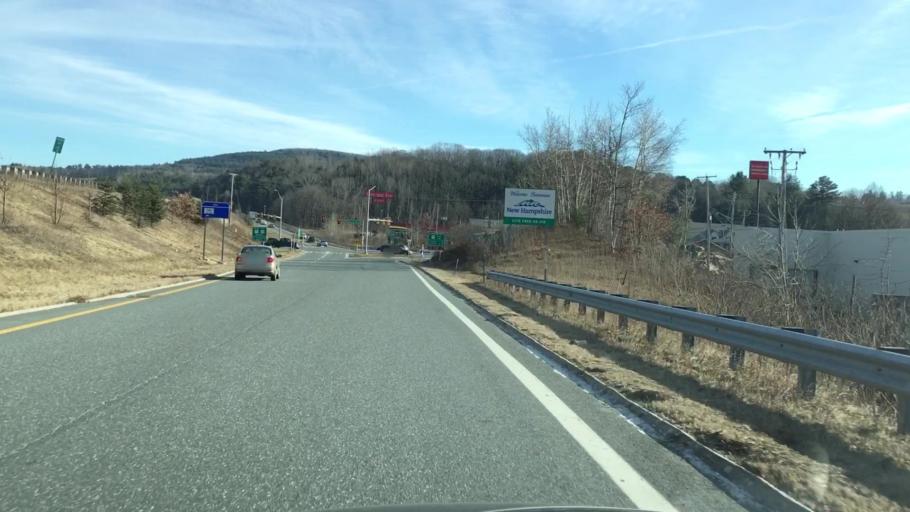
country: US
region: Vermont
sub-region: Windsor County
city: White River Junction
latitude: 43.6316
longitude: -72.3225
